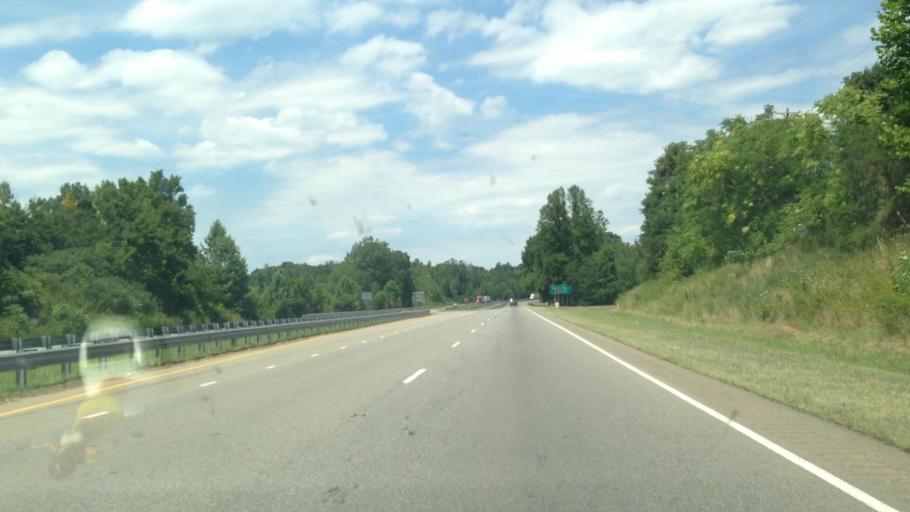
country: US
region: North Carolina
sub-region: Rockingham County
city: Stoneville
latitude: 36.4834
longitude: -79.9244
